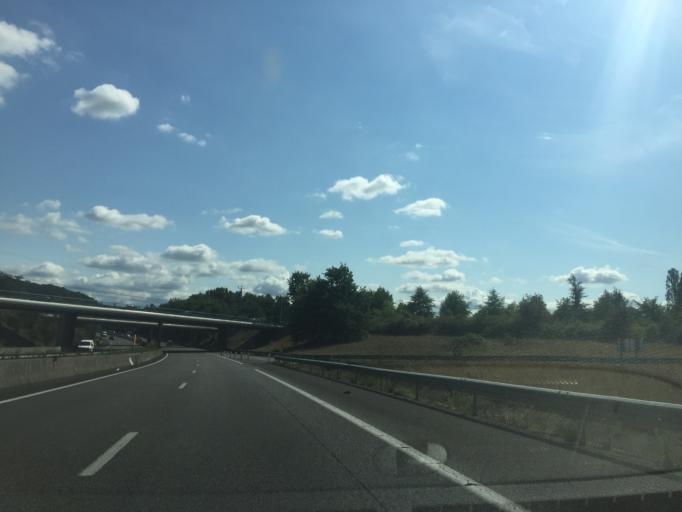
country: FR
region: Midi-Pyrenees
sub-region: Departement de la Haute-Garonne
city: Martres-Tolosane
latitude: 43.1872
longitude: 0.9808
